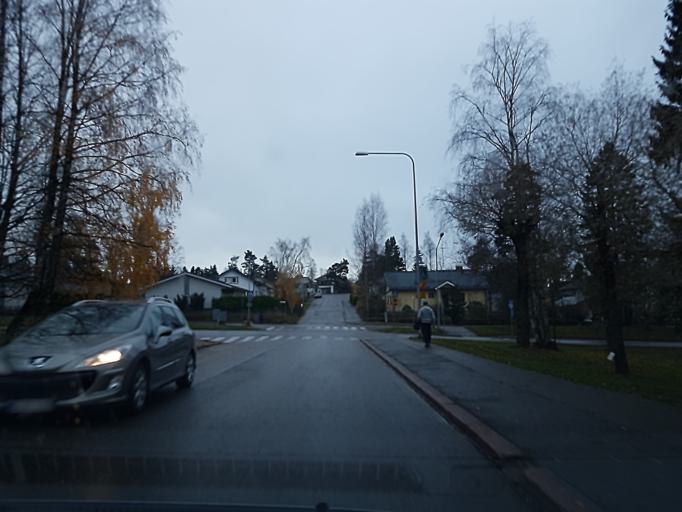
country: FI
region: Uusimaa
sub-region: Helsinki
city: Vantaa
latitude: 60.2374
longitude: 25.1145
